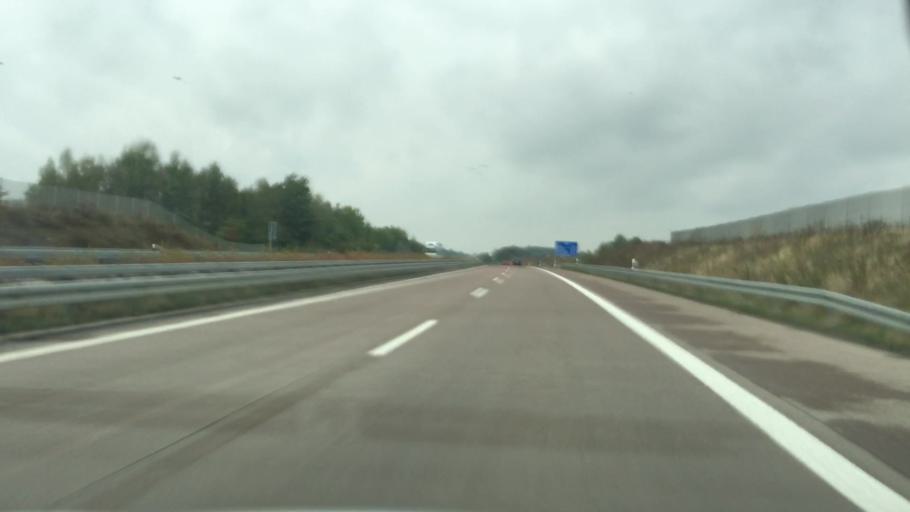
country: DE
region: Saxony
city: Penig
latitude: 50.9500
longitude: 12.6909
